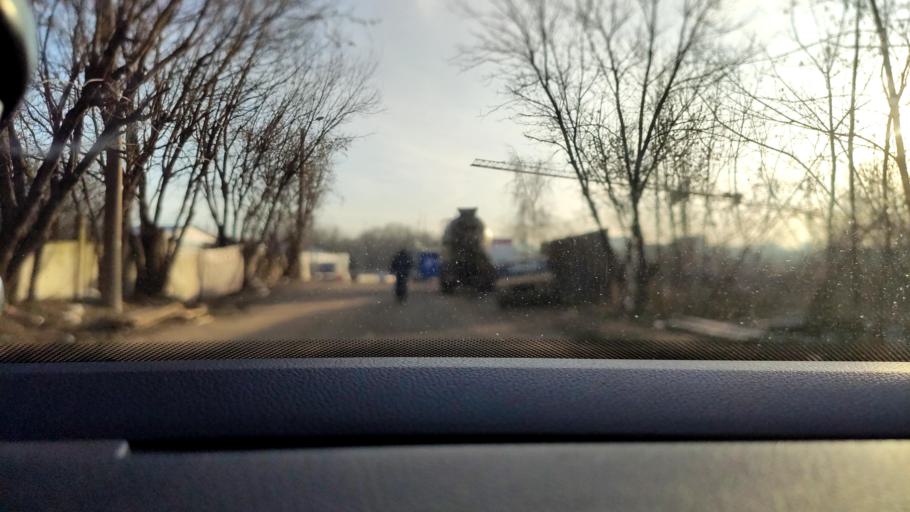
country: RU
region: Moskovskaya
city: Fili
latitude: 55.7500
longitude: 37.4596
